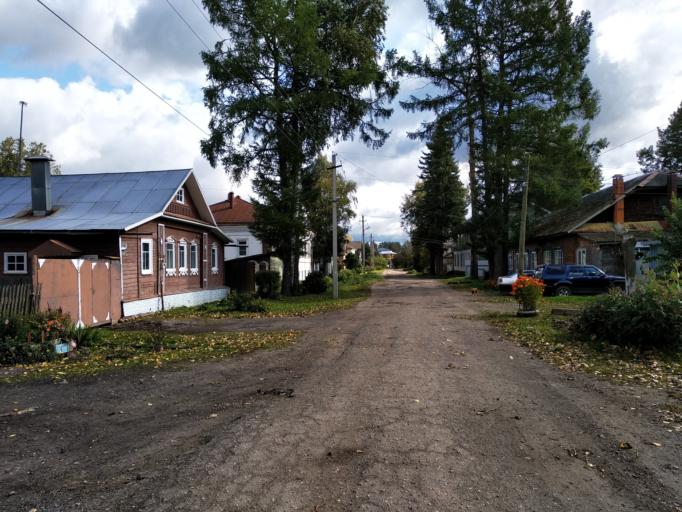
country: RU
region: Tverskaya
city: Kashin
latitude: 57.3619
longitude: 37.6183
